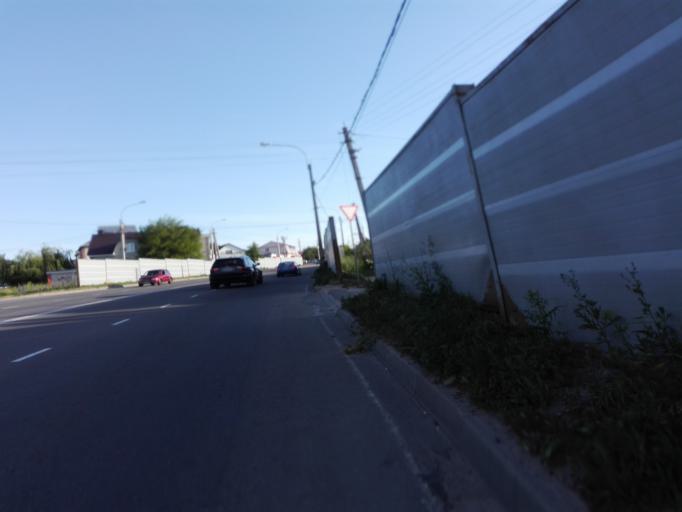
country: RU
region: Orjol
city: Orel
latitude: 52.9516
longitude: 36.0281
